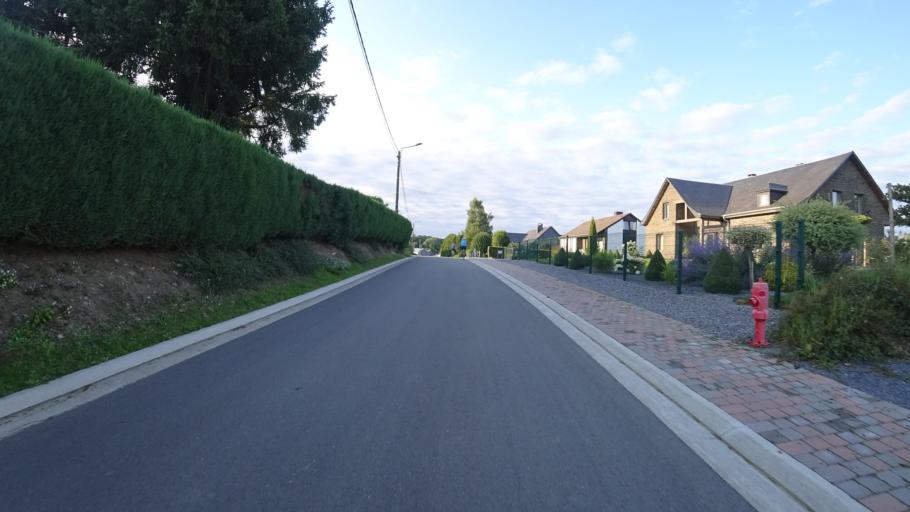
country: BE
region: Wallonia
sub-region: Province du Luxembourg
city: Neufchateau
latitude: 49.8926
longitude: 5.3857
